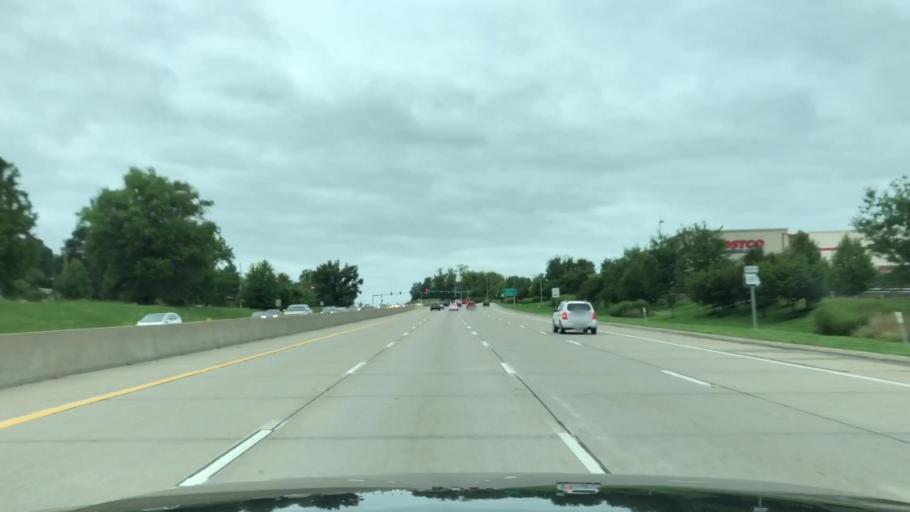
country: US
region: Missouri
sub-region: Saint Louis County
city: Manchester
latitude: 38.5958
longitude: -90.5086
